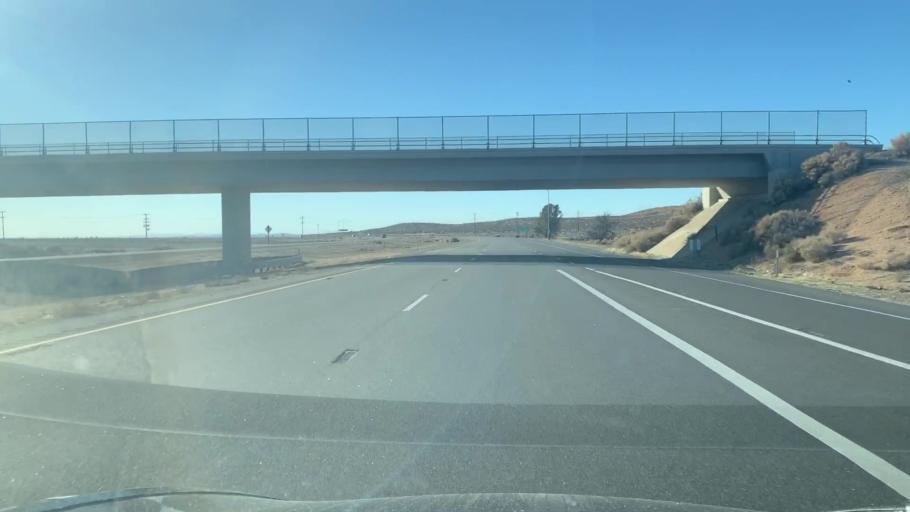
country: US
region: California
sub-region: Kern County
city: Boron
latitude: 35.0099
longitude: -117.6487
